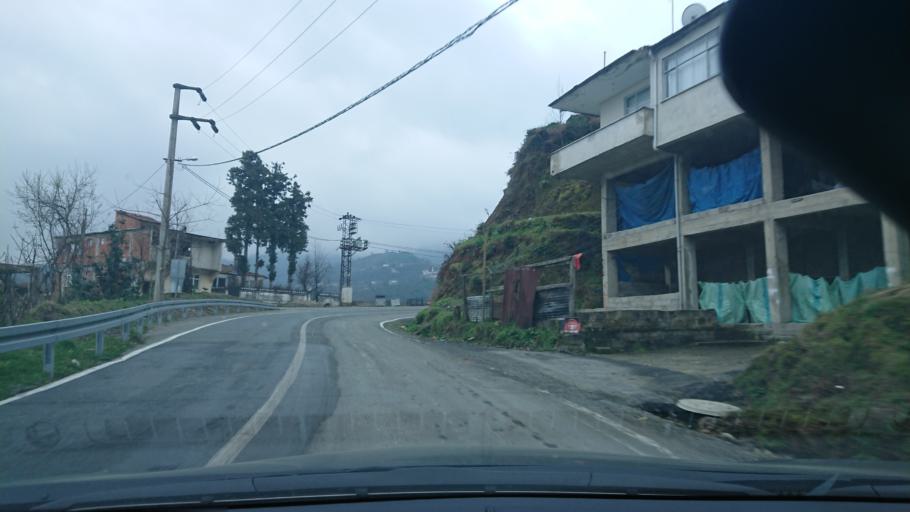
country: TR
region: Rize
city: Rize
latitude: 41.0067
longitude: 40.4881
